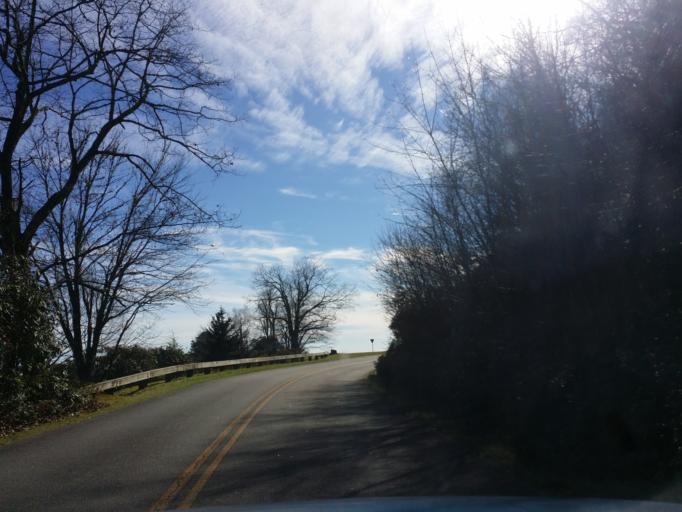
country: US
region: North Carolina
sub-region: Buncombe County
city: Black Mountain
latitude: 35.7193
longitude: -82.2222
